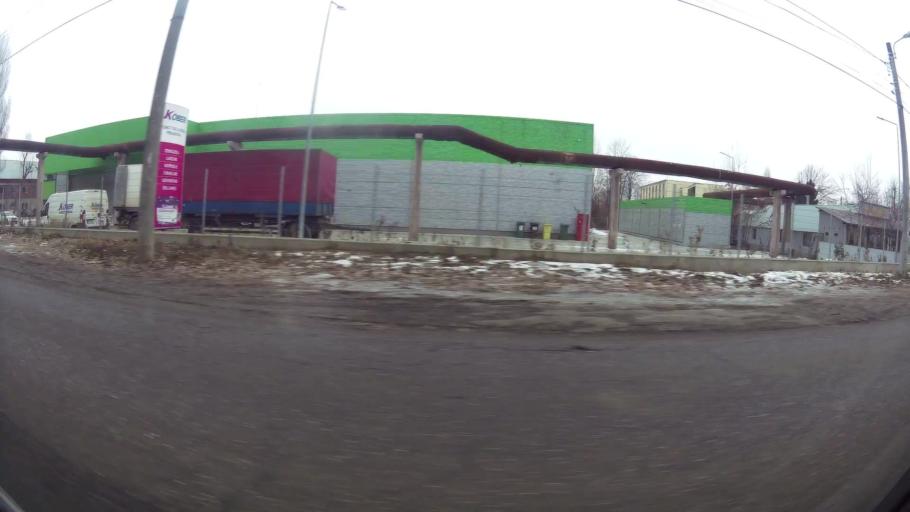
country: RO
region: Prahova
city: Ploiesti
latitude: 44.9397
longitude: 26.0503
